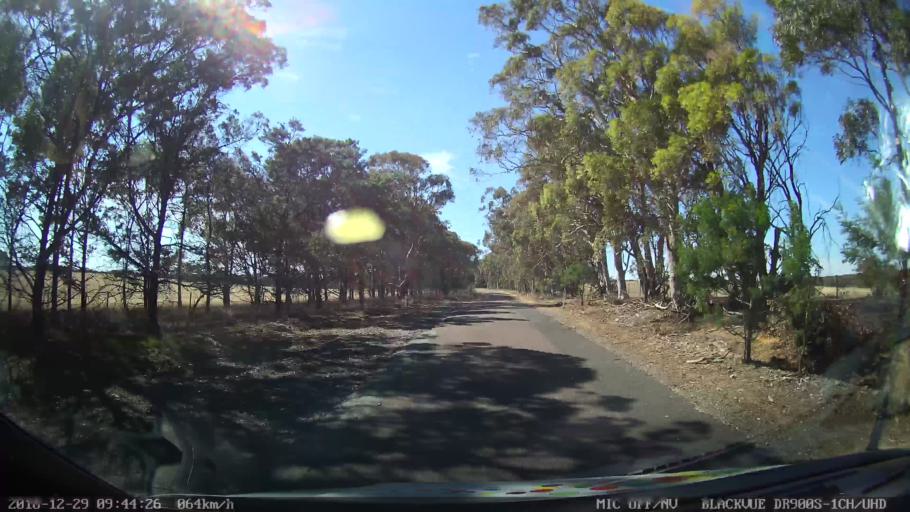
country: AU
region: New South Wales
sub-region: Upper Lachlan Shire
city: Crookwell
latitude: -34.6890
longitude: 149.4265
